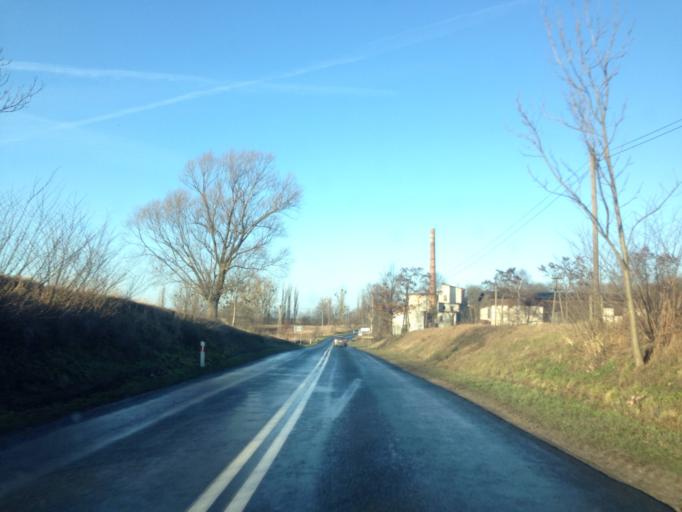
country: PL
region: Kujawsko-Pomorskie
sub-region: Powiat brodnicki
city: Bobrowo
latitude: 53.3414
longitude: 19.2175
